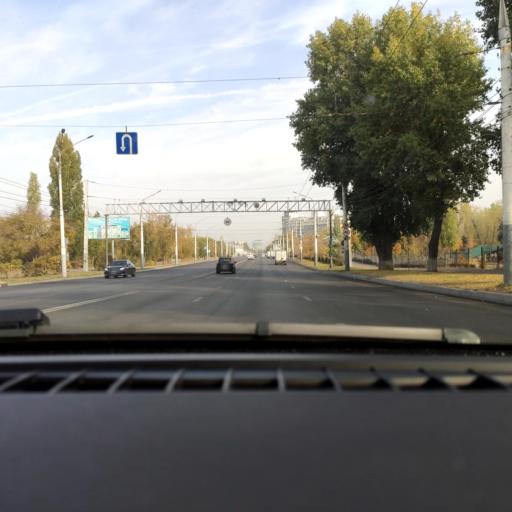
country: RU
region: Voronezj
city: Voronezh
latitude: 51.6580
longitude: 39.2453
